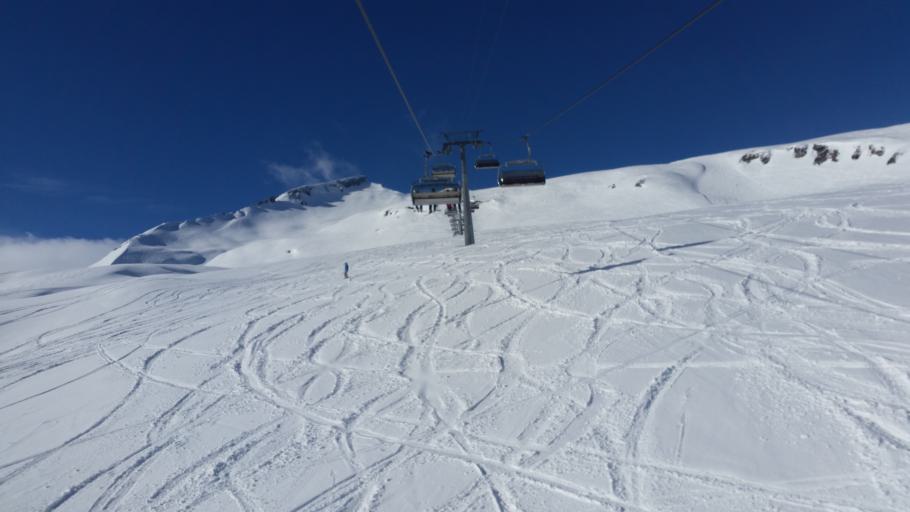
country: CH
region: Grisons
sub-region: Imboden District
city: Flims
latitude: 46.8591
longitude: 9.2267
